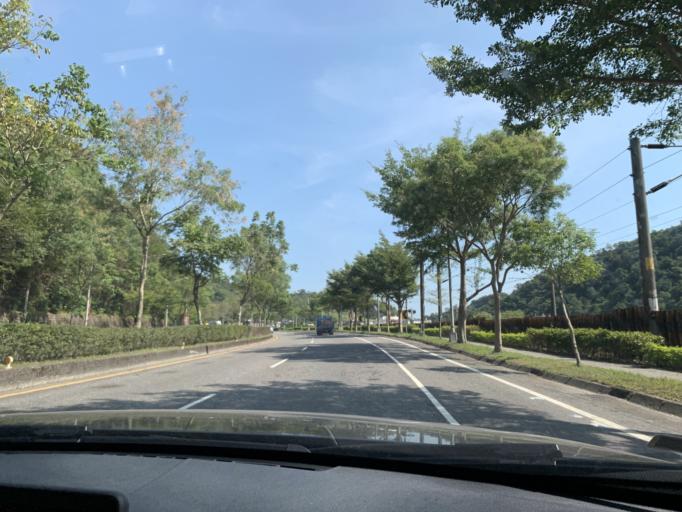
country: TW
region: Taiwan
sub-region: Yilan
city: Yilan
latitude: 24.6008
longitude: 121.8347
